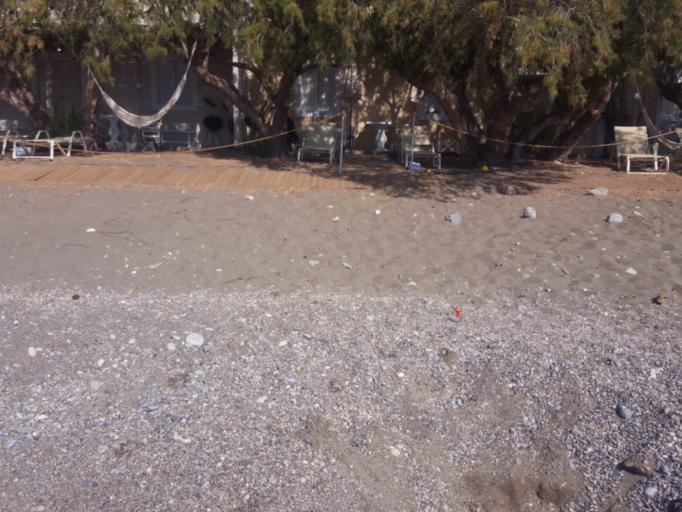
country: GR
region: Crete
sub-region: Nomos Lasithiou
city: Kato Chorio
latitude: 35.0136
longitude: 25.8412
